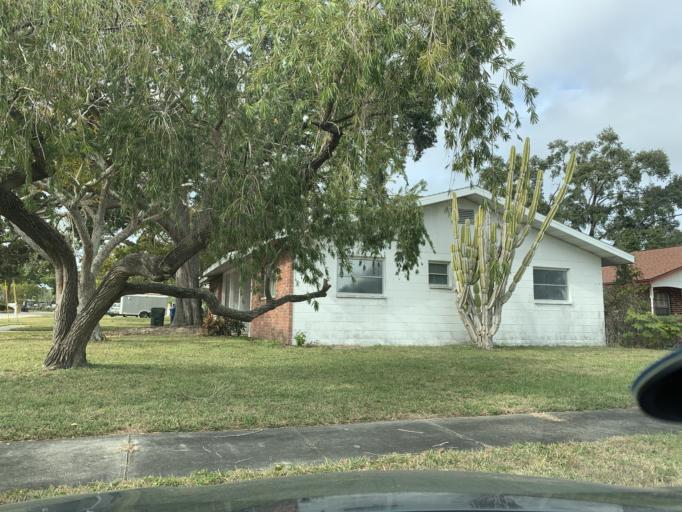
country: US
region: Florida
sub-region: Pinellas County
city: Ridgecrest
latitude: 27.8838
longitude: -82.7831
